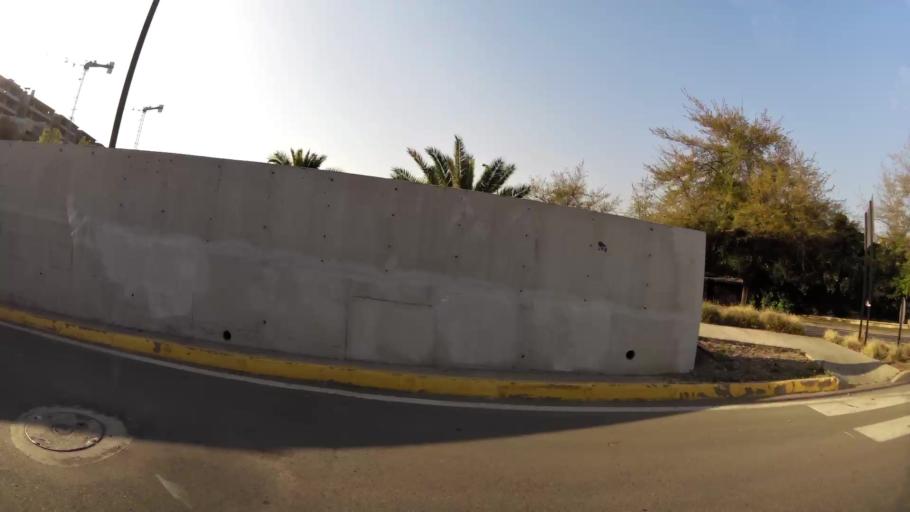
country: CL
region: Santiago Metropolitan
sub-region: Provincia de Santiago
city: Villa Presidente Frei, Nunoa, Santiago, Chile
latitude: -33.3531
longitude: -70.5400
